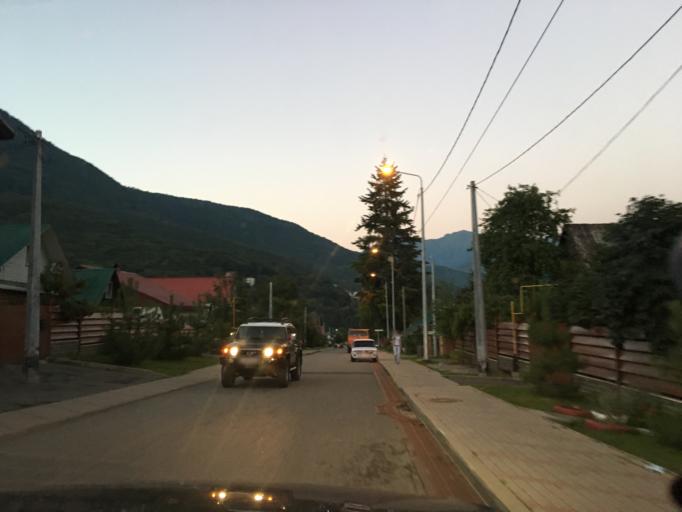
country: RU
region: Krasnodarskiy
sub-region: Sochi City
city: Krasnaya Polyana
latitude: 43.6795
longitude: 40.2069
